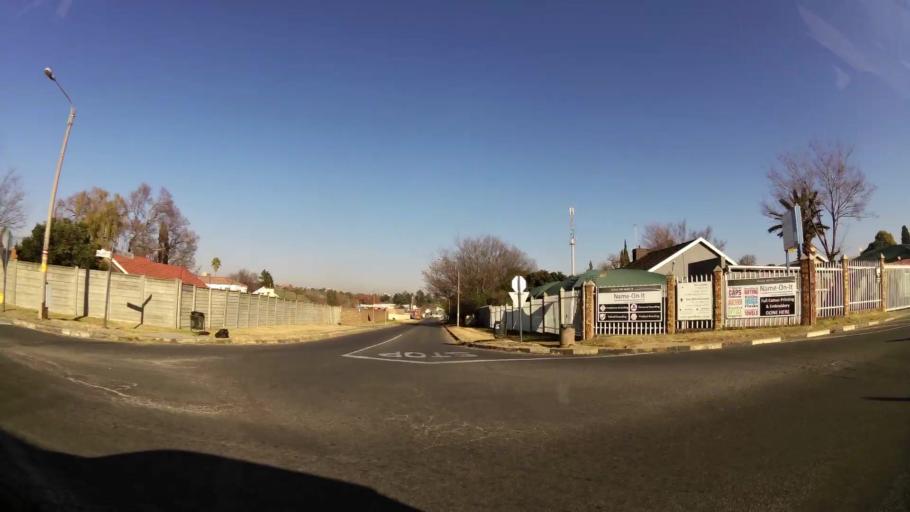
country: ZA
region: Gauteng
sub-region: City of Johannesburg Metropolitan Municipality
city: Modderfontein
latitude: -26.1320
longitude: 28.1653
